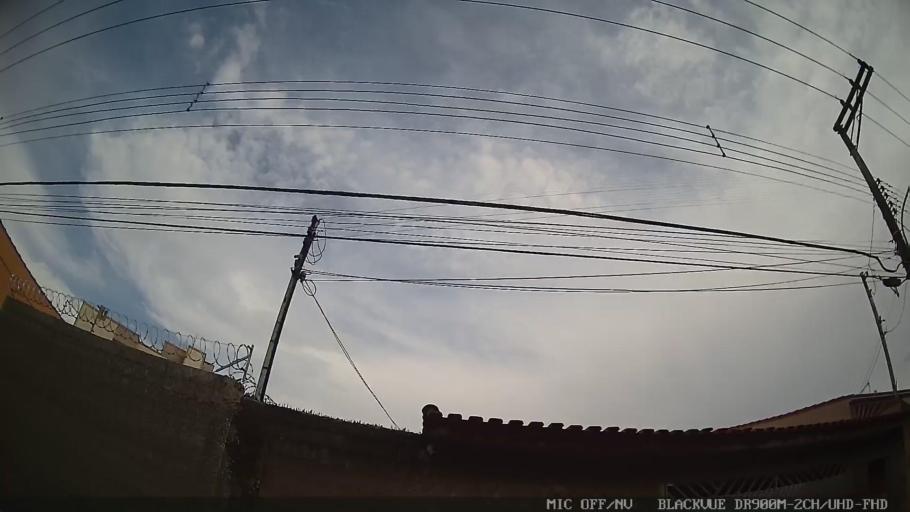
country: BR
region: Sao Paulo
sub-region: Braganca Paulista
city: Braganca Paulista
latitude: -22.9458
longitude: -46.5459
